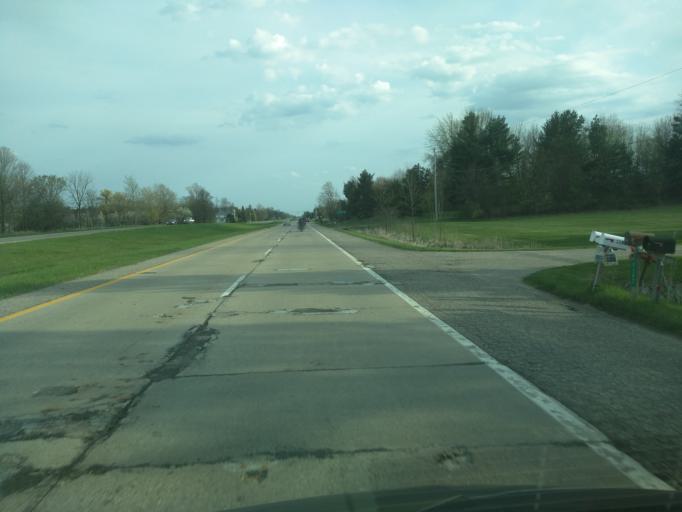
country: US
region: Michigan
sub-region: Eaton County
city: Dimondale
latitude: 42.5852
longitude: -84.6223
